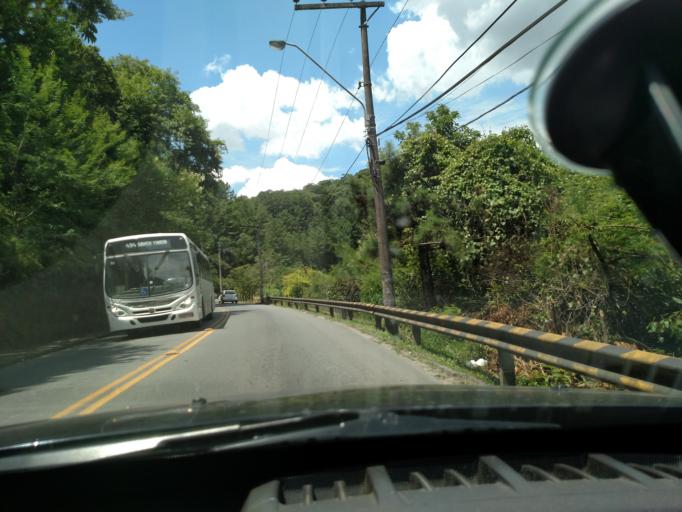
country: BR
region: Santa Catarina
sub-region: Blumenau
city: Blumenau
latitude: -26.9650
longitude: -49.0742
